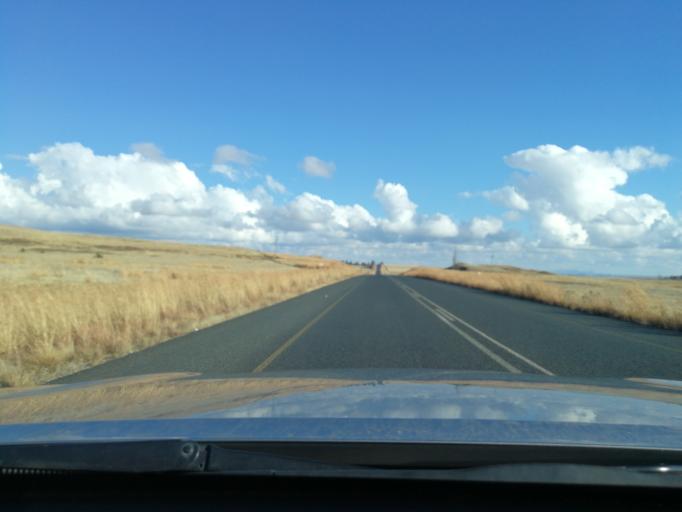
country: ZA
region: Orange Free State
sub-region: Thabo Mofutsanyana District Municipality
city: Bethlehem
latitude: -28.0473
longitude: 28.3671
